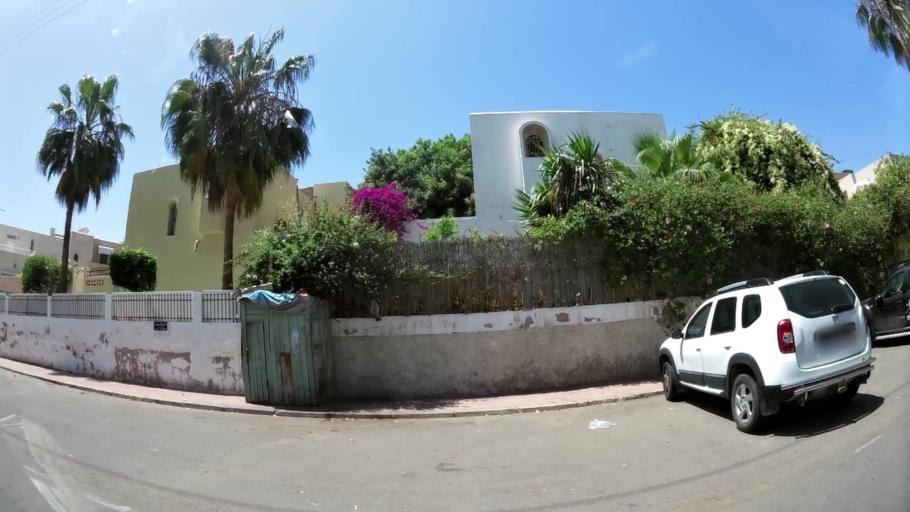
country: MA
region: Souss-Massa-Draa
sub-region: Agadir-Ida-ou-Tnan
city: Agadir
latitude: 30.4318
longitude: -9.5902
